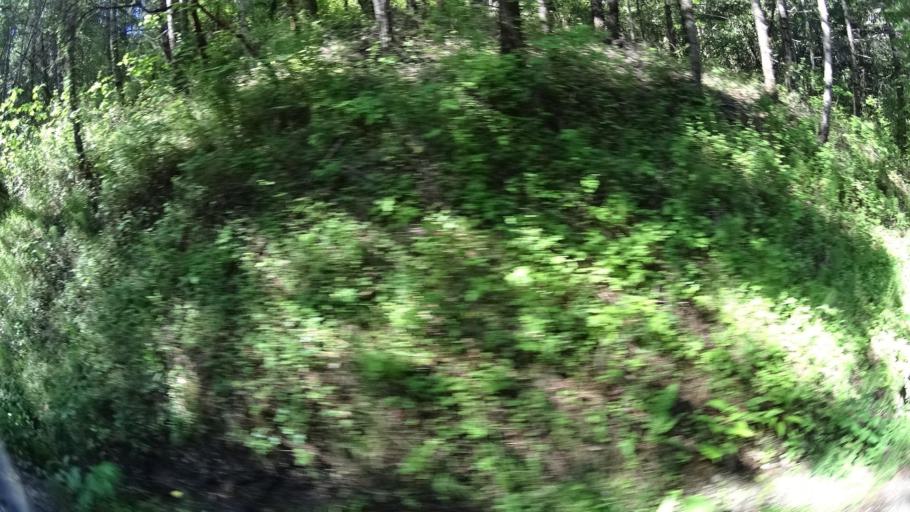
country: US
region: California
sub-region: Humboldt County
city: Rio Dell
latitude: 40.3033
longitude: -124.2550
